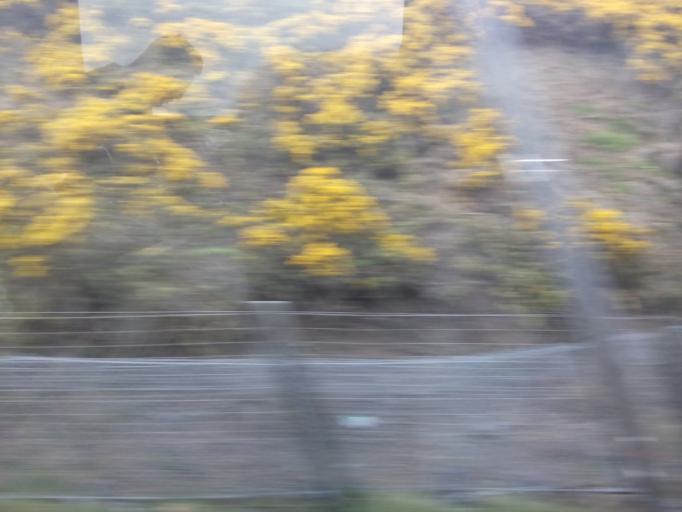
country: GB
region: Scotland
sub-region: The Scottish Borders
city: Eyemouth
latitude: 55.8326
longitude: -2.0597
